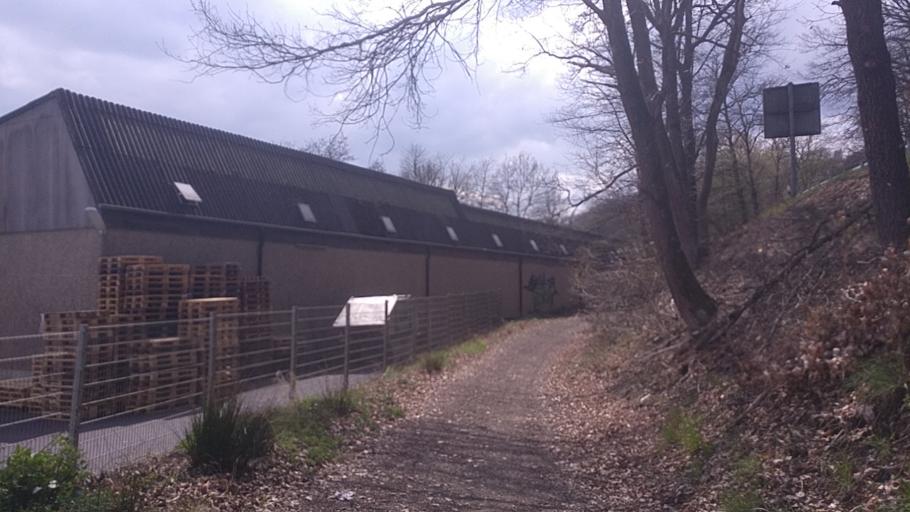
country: DE
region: Rheinland-Pfalz
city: Peterslahr
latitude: 50.6247
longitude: 7.4260
